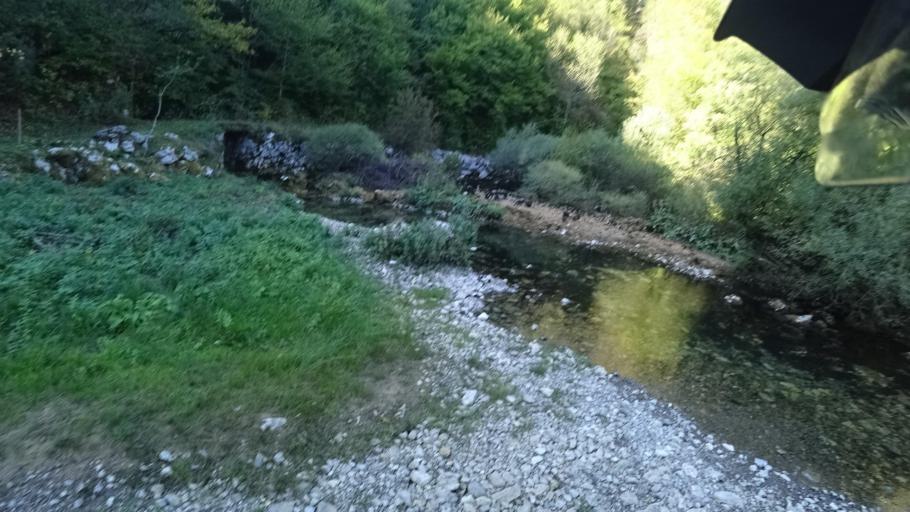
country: HR
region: Karlovacka
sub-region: Grad Ogulin
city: Ogulin
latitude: 45.2912
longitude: 15.1405
